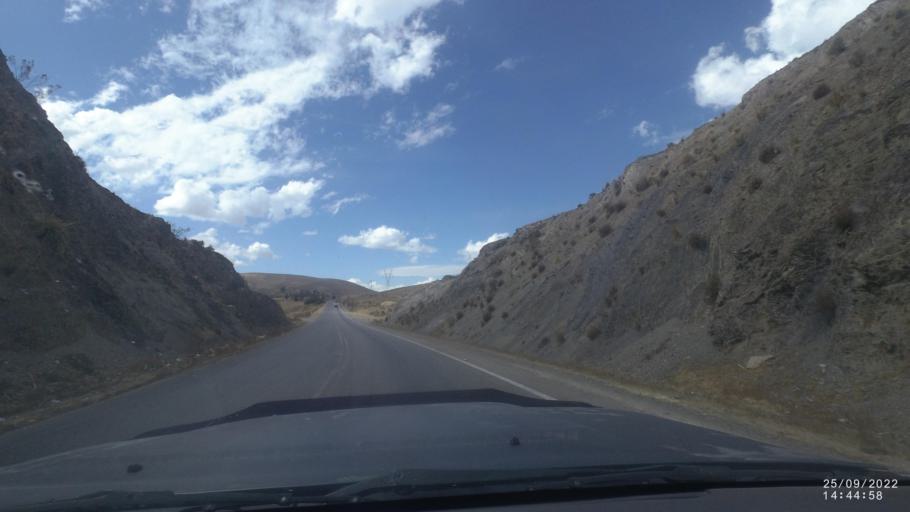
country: BO
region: Cochabamba
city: Irpa Irpa
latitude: -17.7090
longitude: -66.5265
